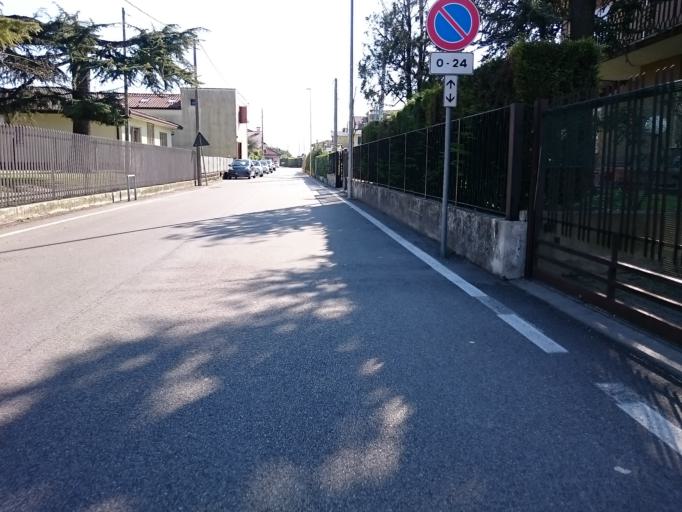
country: IT
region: Veneto
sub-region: Provincia di Padova
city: Ponte San Nicolo
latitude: 45.3767
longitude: 11.9093
